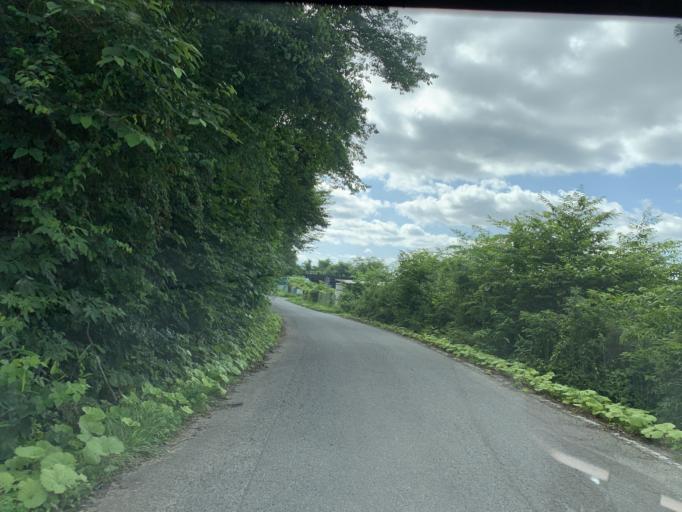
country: JP
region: Iwate
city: Ichinoseki
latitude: 38.9270
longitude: 141.0501
